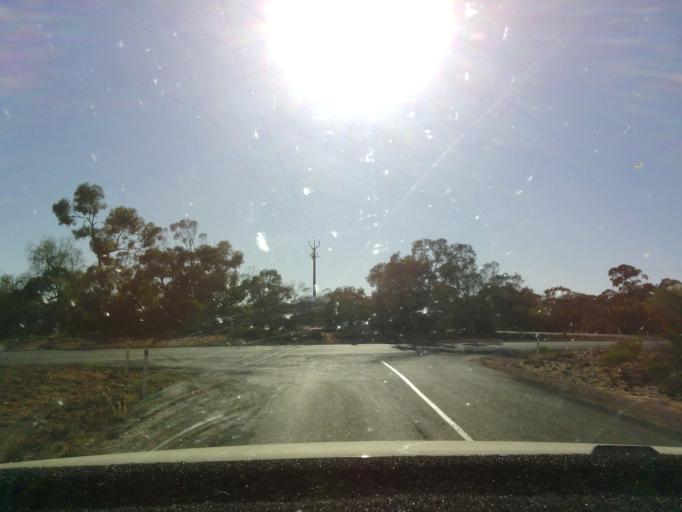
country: AU
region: South Australia
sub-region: Berri and Barmera
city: Monash
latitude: -34.2253
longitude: 140.5738
